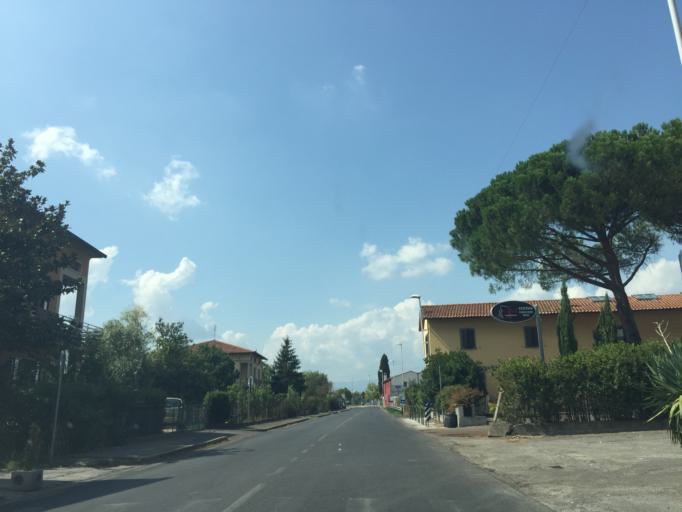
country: IT
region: Tuscany
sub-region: Provincia di Prato
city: Seano
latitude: 43.8348
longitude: 11.0288
